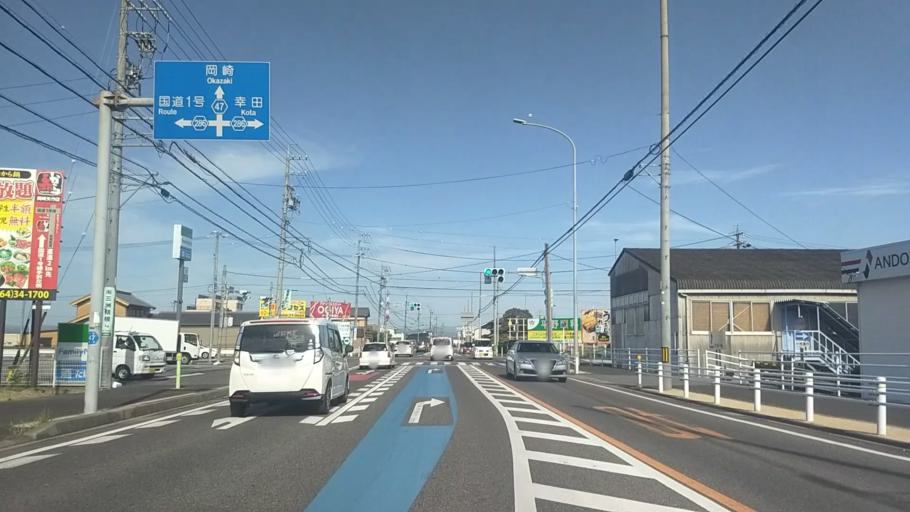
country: JP
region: Aichi
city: Anjo
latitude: 34.9583
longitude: 137.0997
